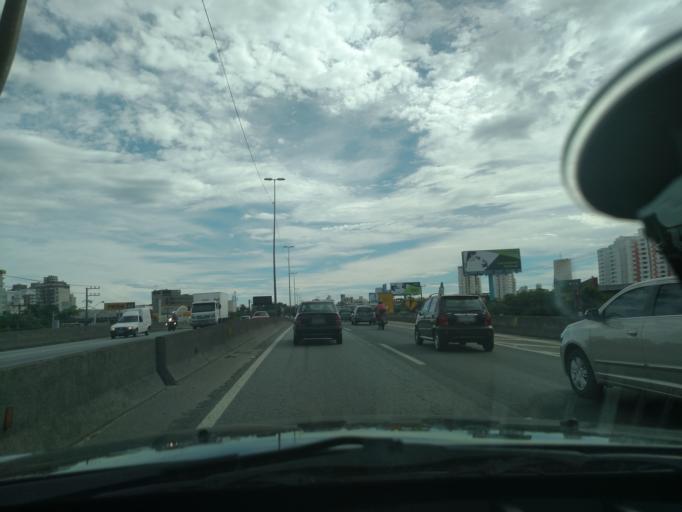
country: BR
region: Santa Catarina
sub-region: Sao Jose
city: Campinas
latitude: -27.5814
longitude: -48.6146
